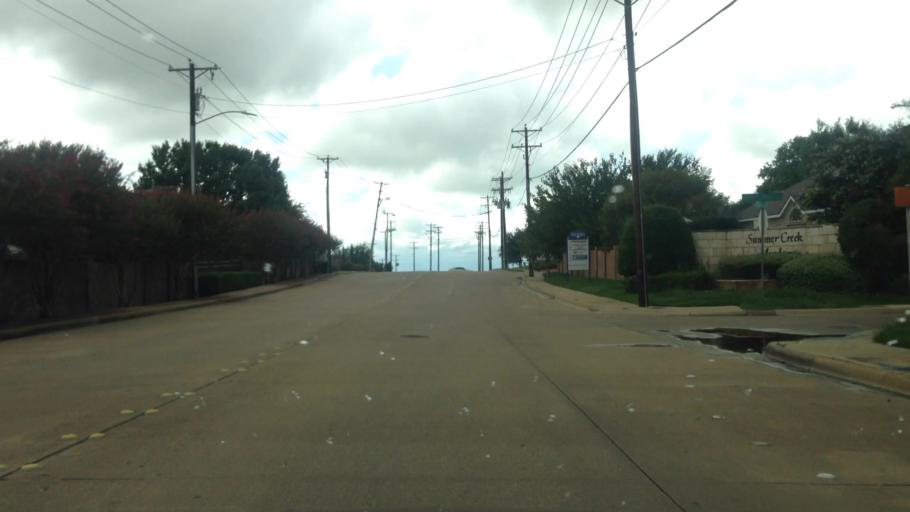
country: US
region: Texas
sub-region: Tarrant County
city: Crowley
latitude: 32.6287
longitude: -97.4046
